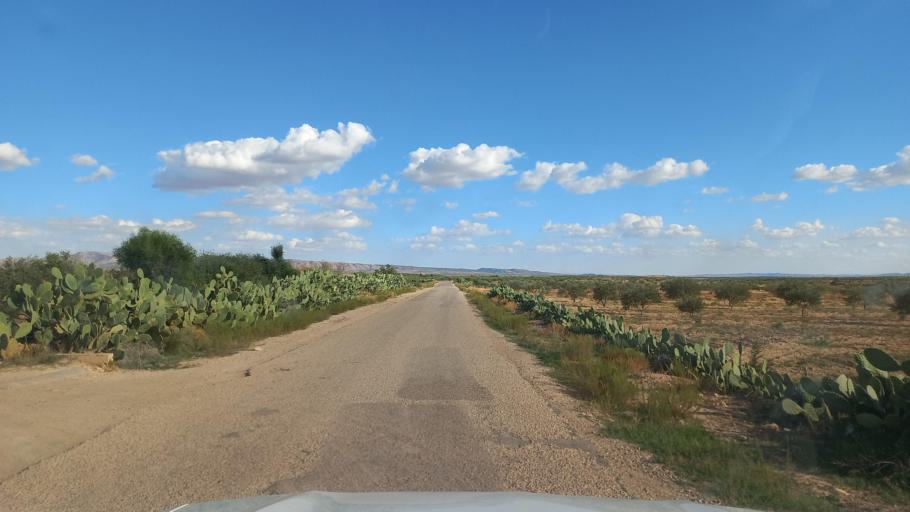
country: TN
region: Al Qasrayn
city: Sbiba
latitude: 35.3883
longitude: 9.0287
